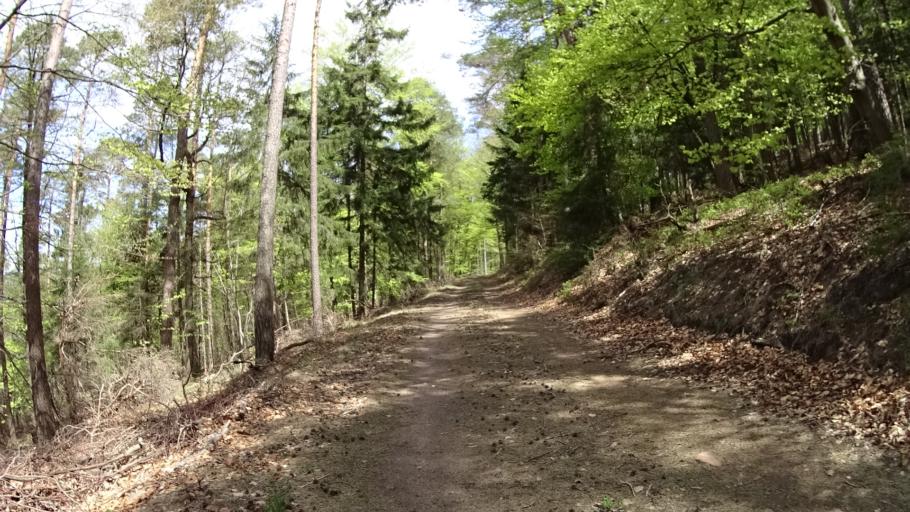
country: DE
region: Rheinland-Pfalz
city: Ramberg
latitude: 49.3103
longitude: 8.0039
